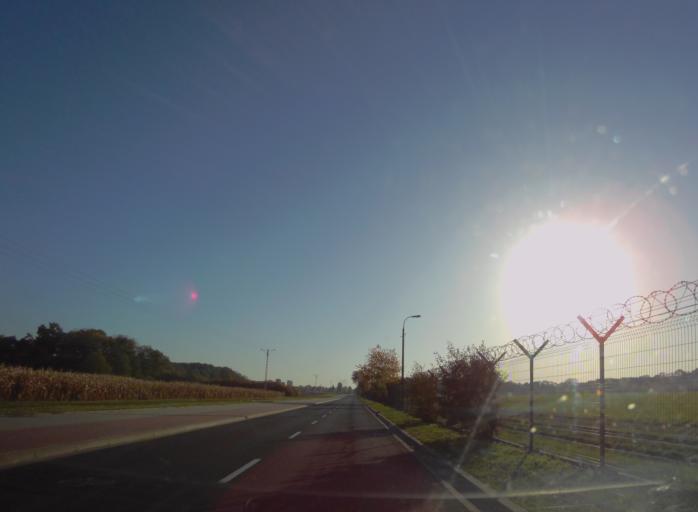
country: PL
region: Masovian Voivodeship
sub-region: Powiat pruszkowski
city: Otrebusy
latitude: 52.1537
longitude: 20.7704
